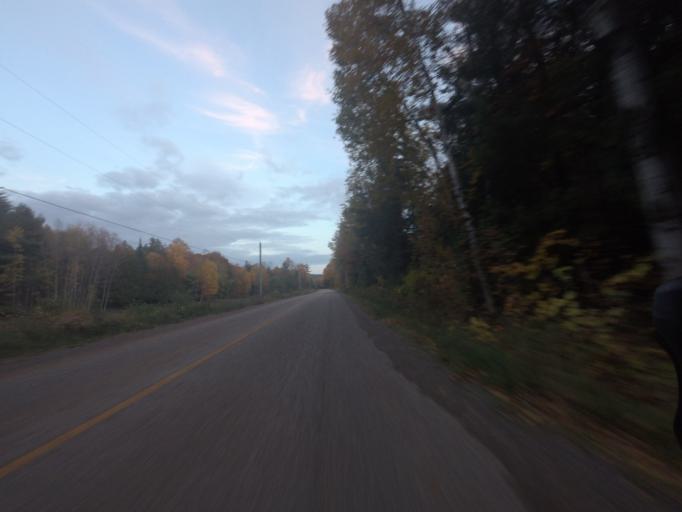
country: CA
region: Ontario
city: Renfrew
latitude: 45.3528
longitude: -76.9507
